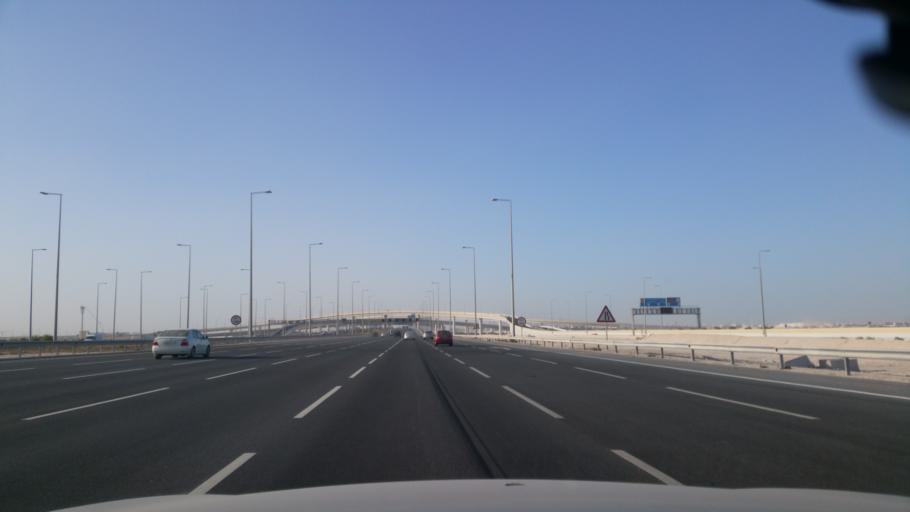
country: QA
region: Al Wakrah
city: Al Wukayr
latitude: 25.1943
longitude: 51.5446
